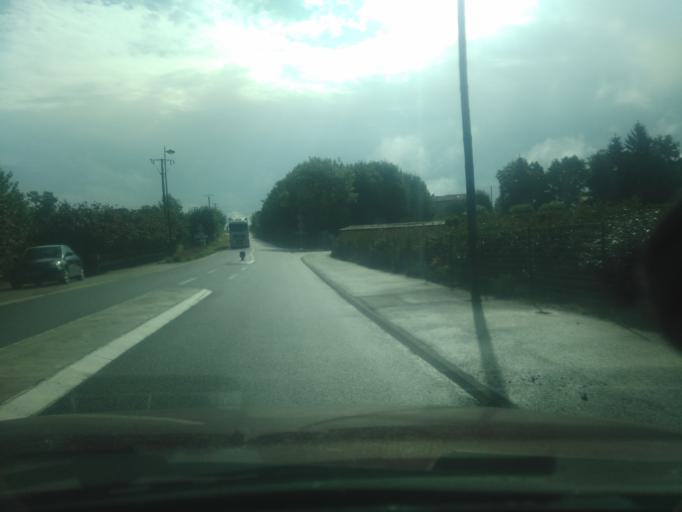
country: FR
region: Poitou-Charentes
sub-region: Departement des Deux-Sevres
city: Saint-Aubin-le-Cloud
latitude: 46.6235
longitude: -0.3440
